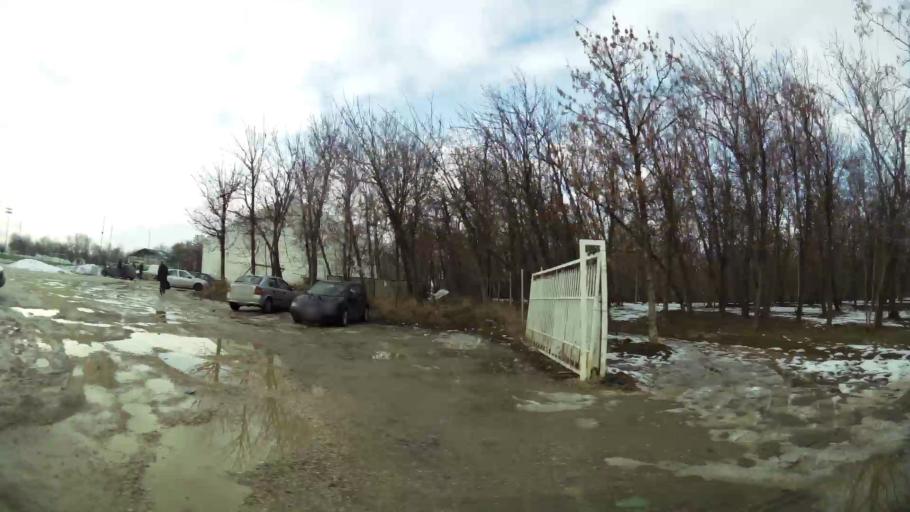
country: XK
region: Pristina
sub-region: Komuna e Prishtines
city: Pristina
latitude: 42.6673
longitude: 21.1519
